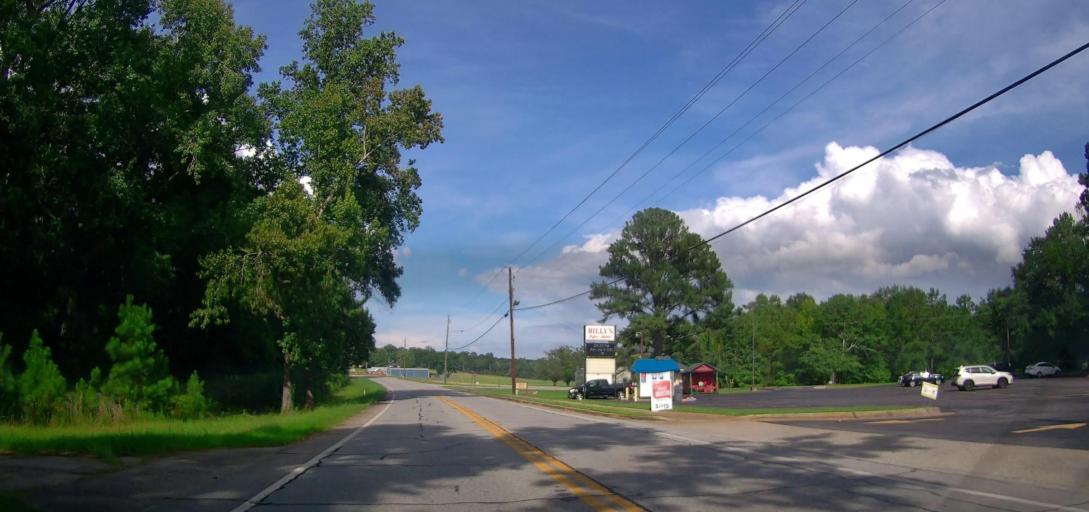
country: US
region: Georgia
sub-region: Harris County
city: Hamilton
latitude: 32.6495
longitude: -84.8742
